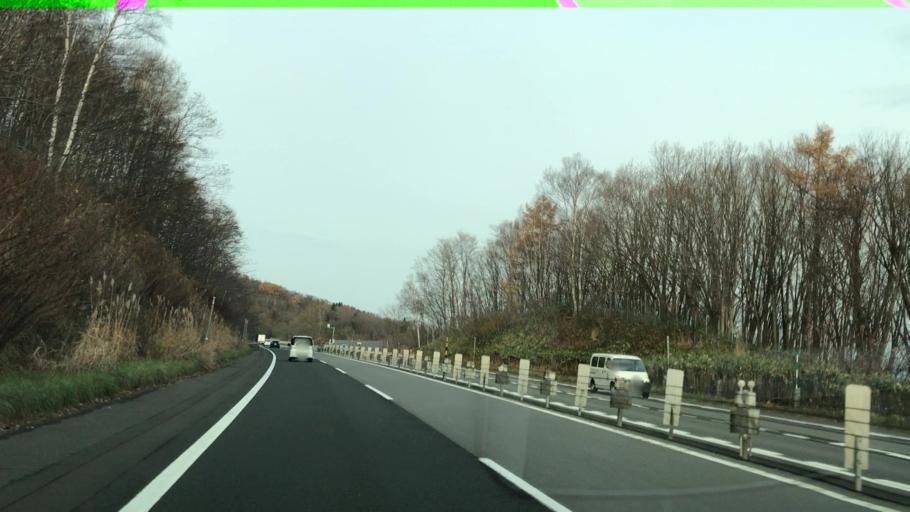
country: JP
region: Hokkaido
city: Otaru
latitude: 43.1448
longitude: 141.1394
